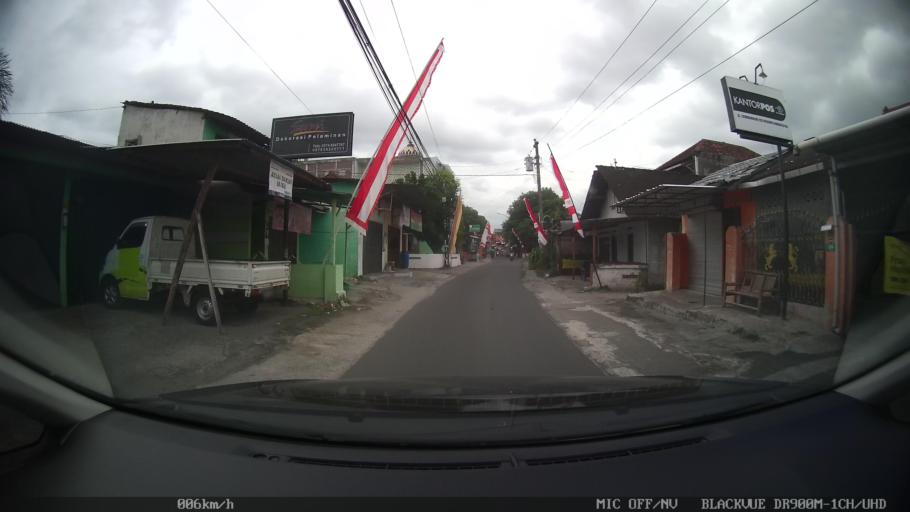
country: ID
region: Daerah Istimewa Yogyakarta
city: Depok
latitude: -7.8048
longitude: 110.4159
